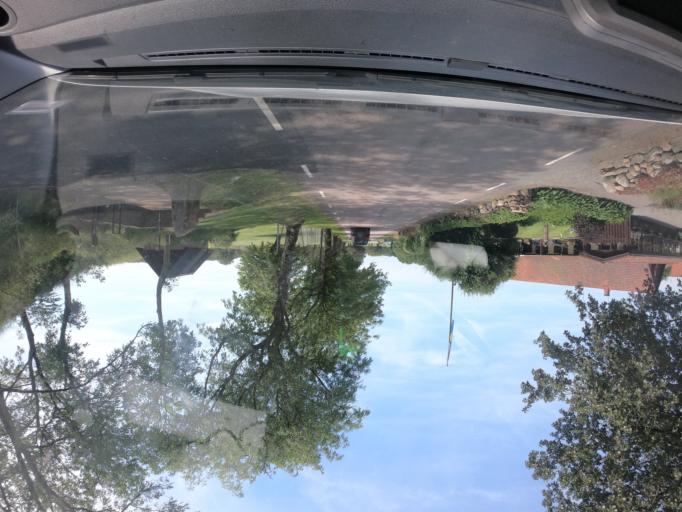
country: SE
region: Skane
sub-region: Bastads Kommun
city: Bastad
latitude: 56.4287
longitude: 12.7887
